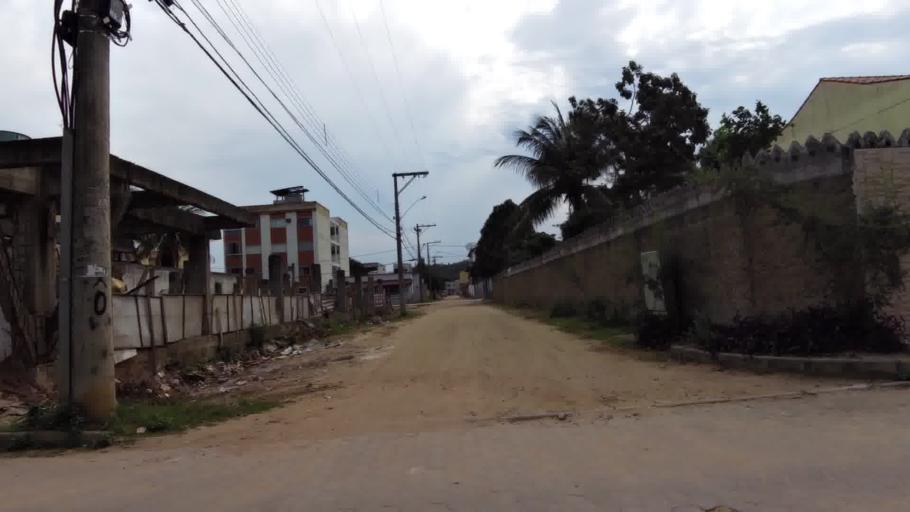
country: BR
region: Espirito Santo
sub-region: Piuma
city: Piuma
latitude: -20.8411
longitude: -40.7302
